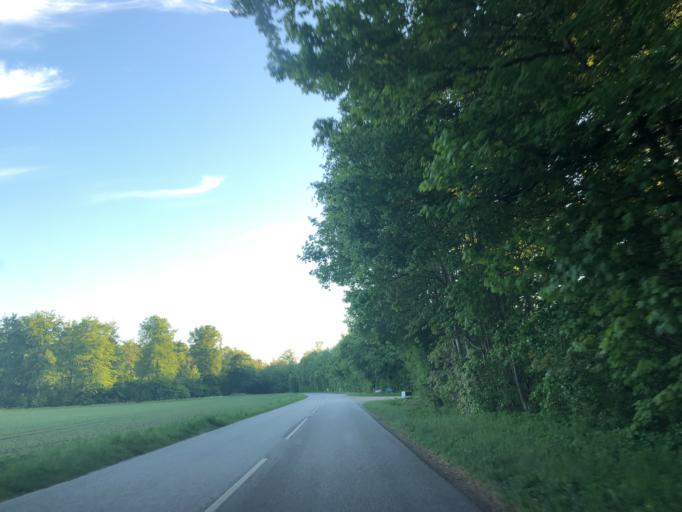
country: DK
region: Zealand
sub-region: Koge Kommune
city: Borup
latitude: 55.4358
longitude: 11.9421
